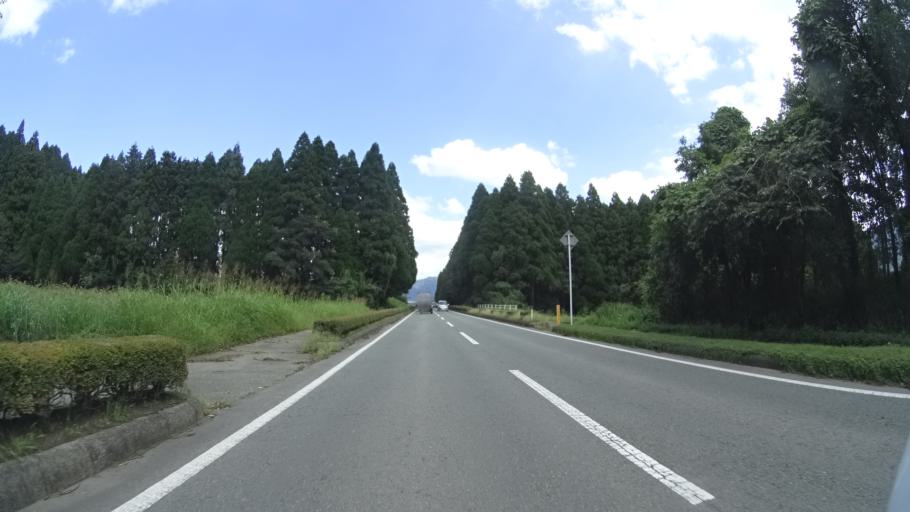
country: JP
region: Kumamoto
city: Aso
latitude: 32.8307
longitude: 131.0856
